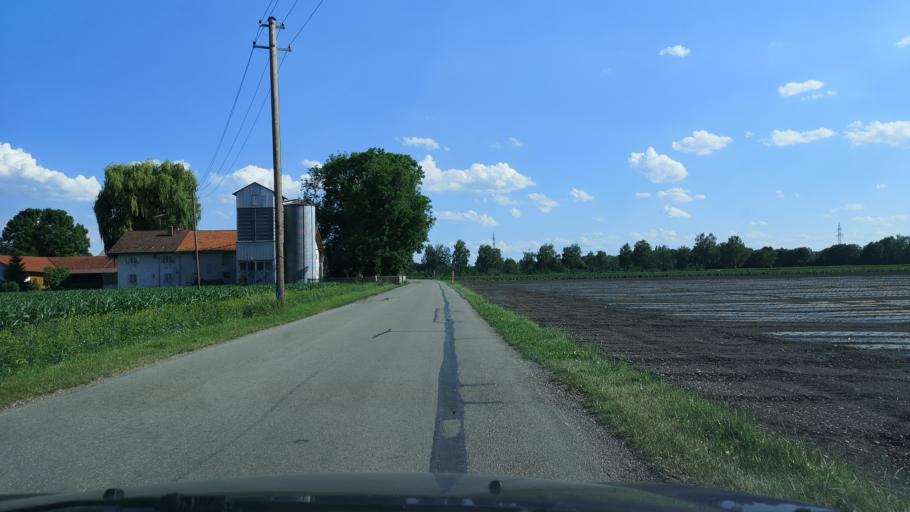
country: DE
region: Bavaria
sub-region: Upper Bavaria
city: Eichenried
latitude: 48.2385
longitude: 11.7820
